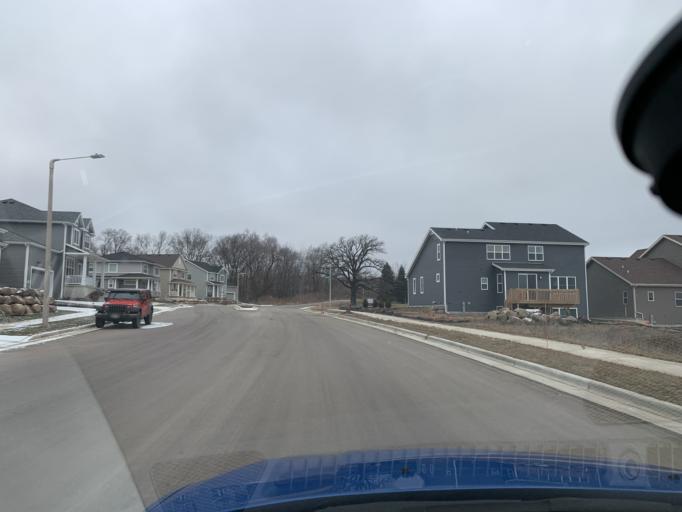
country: US
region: Wisconsin
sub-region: Dane County
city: Middleton
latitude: 43.0705
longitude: -89.5625
